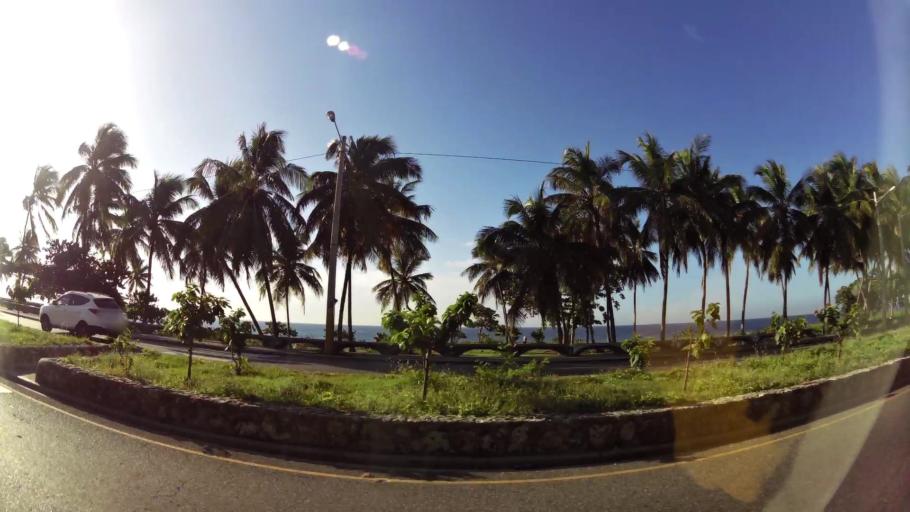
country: DO
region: Santo Domingo
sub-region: Santo Domingo
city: Santo Domingo Este
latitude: 18.4686
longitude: -69.8371
